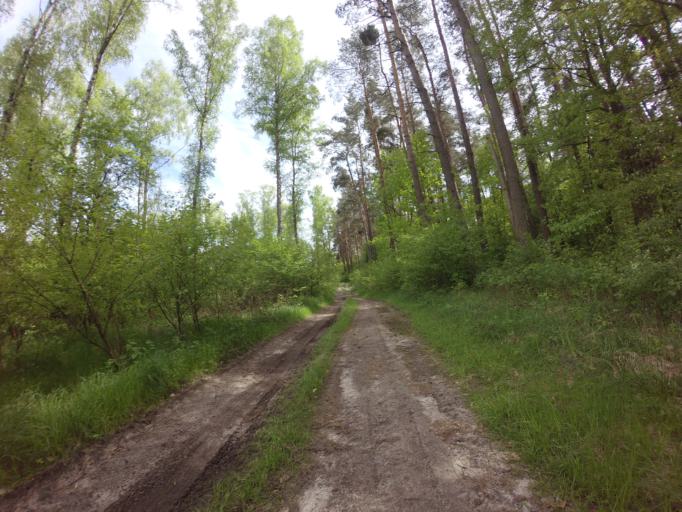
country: PL
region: West Pomeranian Voivodeship
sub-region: Powiat choszczenski
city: Drawno
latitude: 53.1577
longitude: 15.6574
